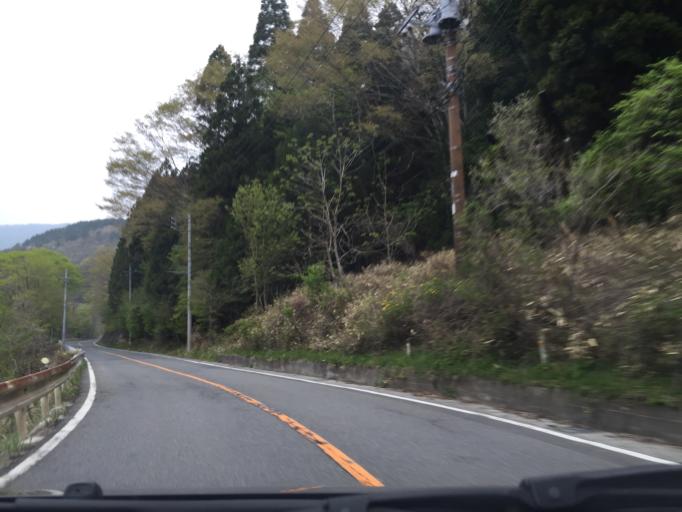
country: JP
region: Tochigi
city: Nikko
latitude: 36.9635
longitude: 139.6962
